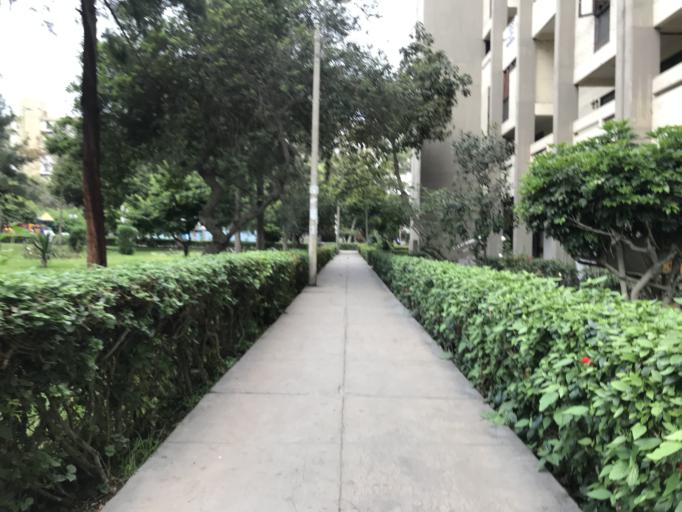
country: PE
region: Lima
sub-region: Lima
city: San Isidro
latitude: -12.0867
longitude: -77.0532
